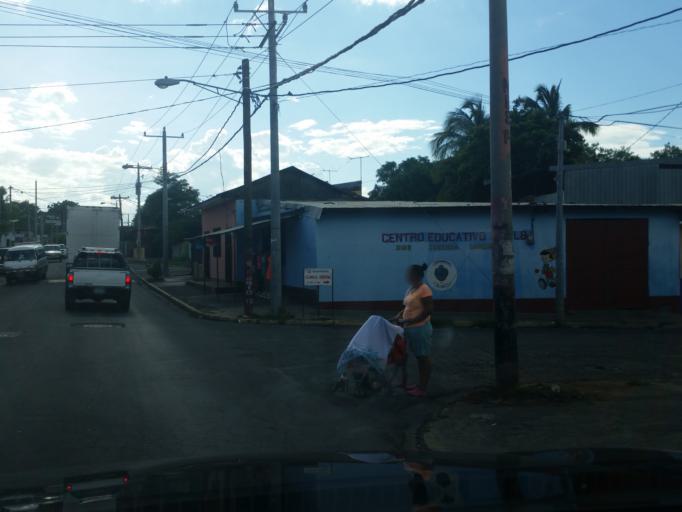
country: NI
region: Managua
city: Managua
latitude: 12.1554
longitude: -86.2923
